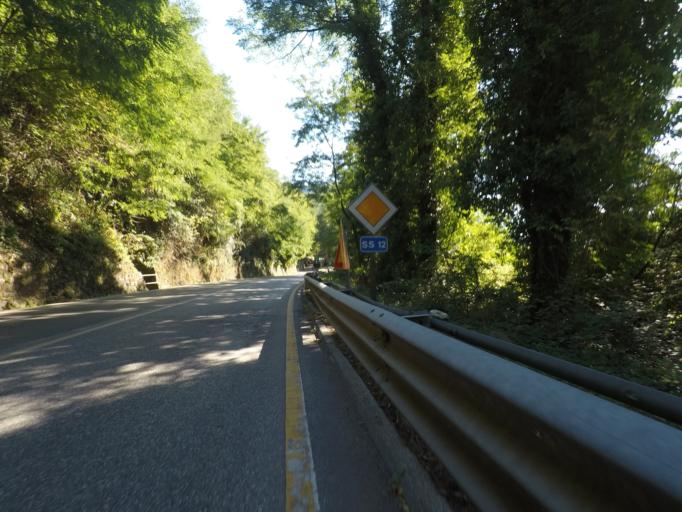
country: IT
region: Tuscany
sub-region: Provincia di Lucca
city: Borgo a Mozzano
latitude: 43.9781
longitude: 10.5512
